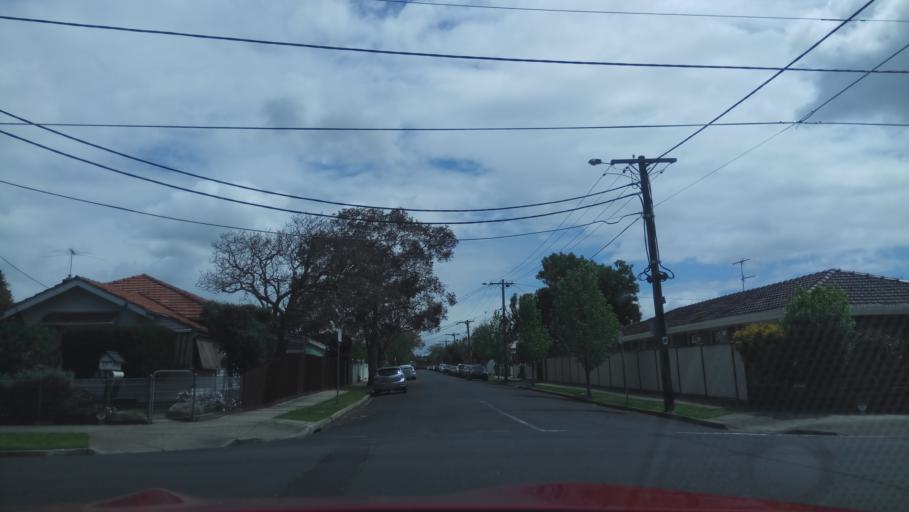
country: AU
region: Victoria
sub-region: Hobsons Bay
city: Newport
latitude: -37.8425
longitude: 144.8875
